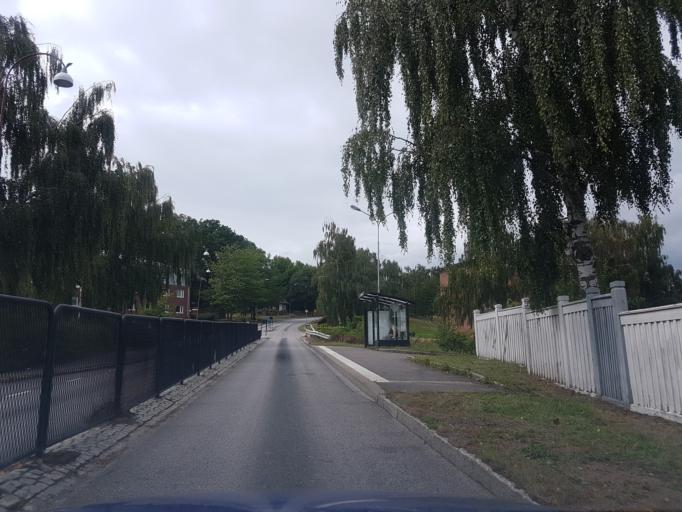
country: SE
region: Vaestra Goetaland
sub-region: Harryda Kommun
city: Molnlycke
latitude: 57.6620
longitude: 12.1151
